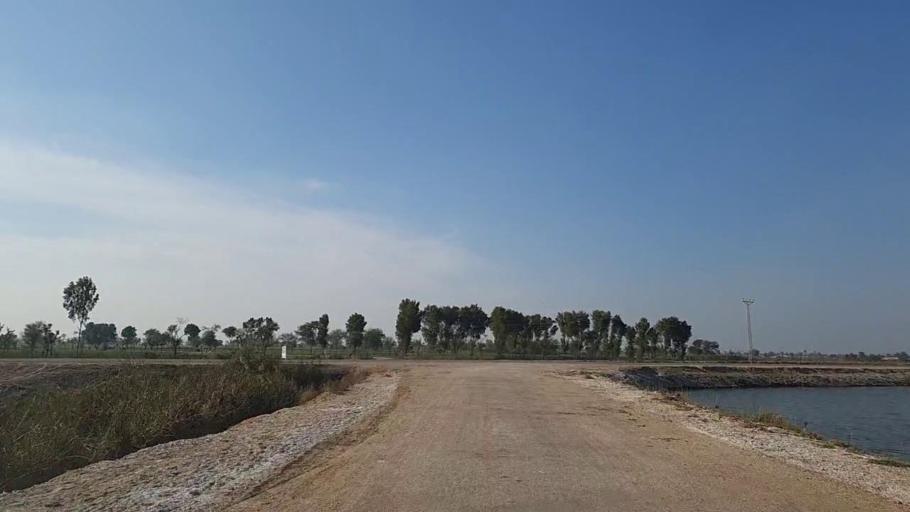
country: PK
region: Sindh
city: Bandhi
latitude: 26.6114
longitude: 68.3088
